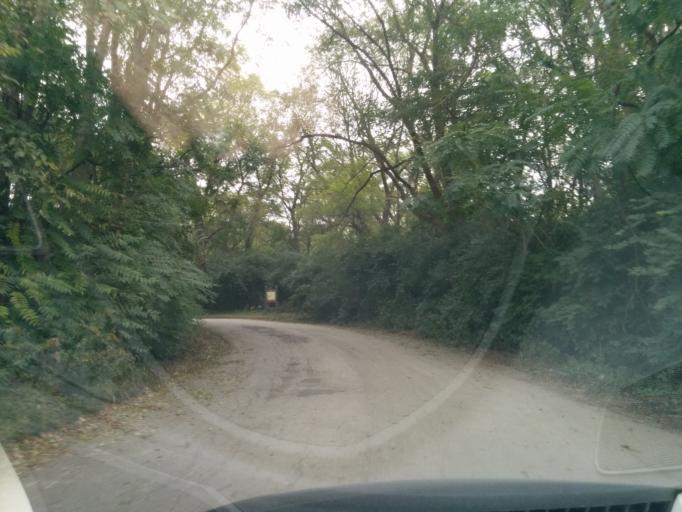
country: US
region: Illinois
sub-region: DuPage County
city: Burr Ridge
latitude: 41.7134
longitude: -87.9130
